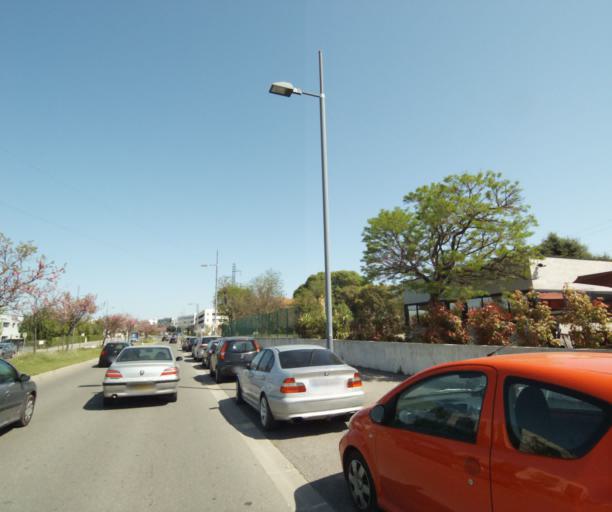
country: FR
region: Languedoc-Roussillon
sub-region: Departement de l'Herault
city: Castelnau-le-Lez
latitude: 43.6128
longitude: 3.9149
